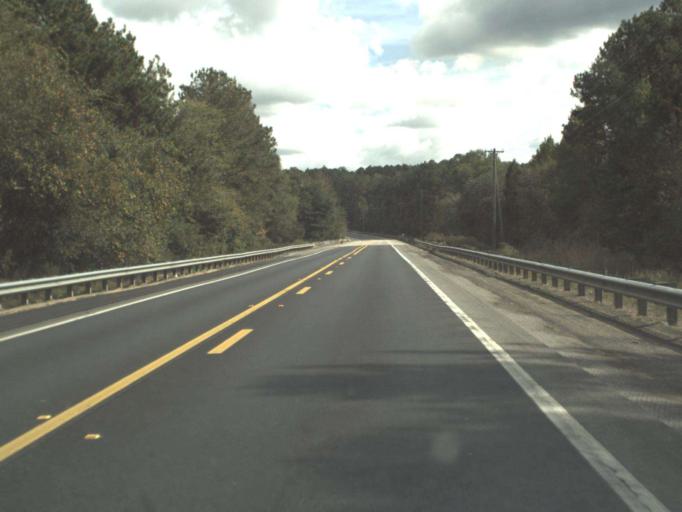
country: US
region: Florida
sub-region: Gadsden County
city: Quincy
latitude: 30.5883
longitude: -84.4986
